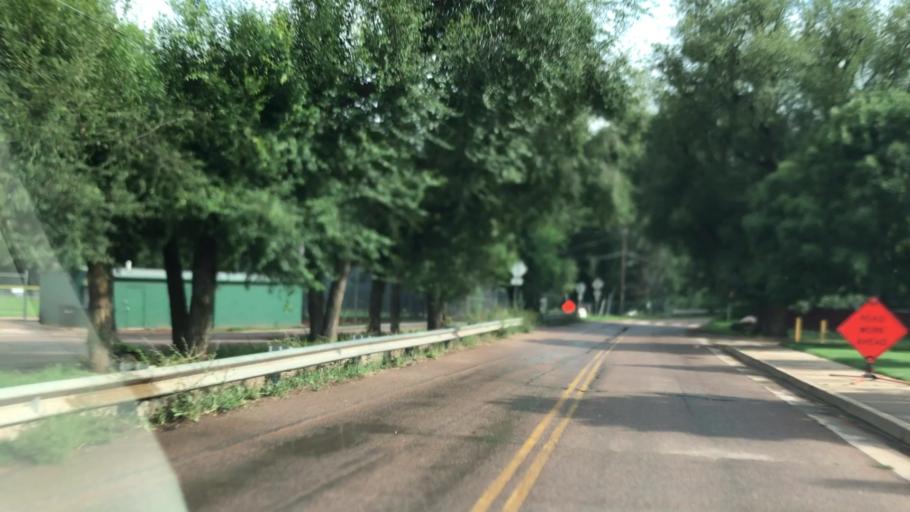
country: US
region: Colorado
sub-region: El Paso County
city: Manitou Springs
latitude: 38.8591
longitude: -104.8914
